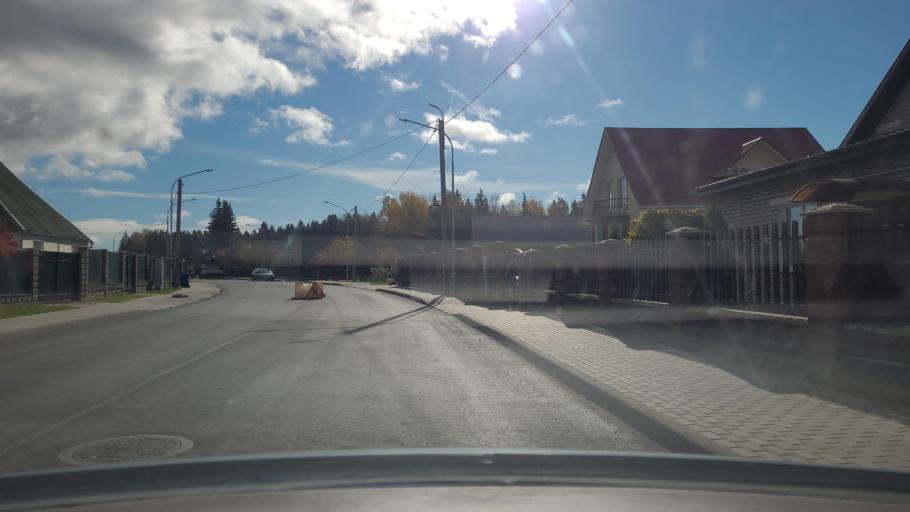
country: BY
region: Grodnenskaya
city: Astravyets
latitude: 54.6085
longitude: 25.9621
